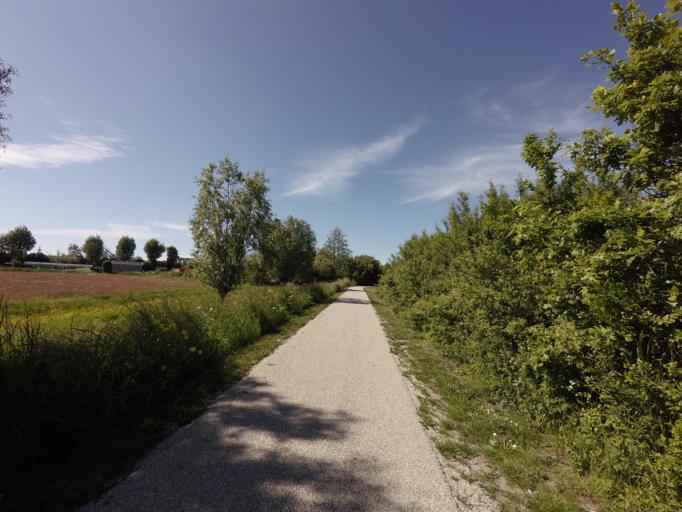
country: NL
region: North Holland
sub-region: Gemeente Uitgeest
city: Uitgeest
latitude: 52.5268
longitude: 4.7284
